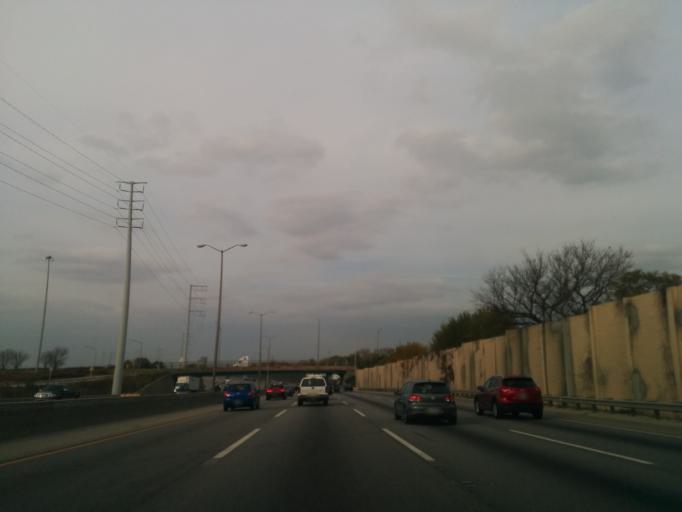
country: US
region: Illinois
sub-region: Cook County
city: Berkeley
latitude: 41.8879
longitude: -87.9183
